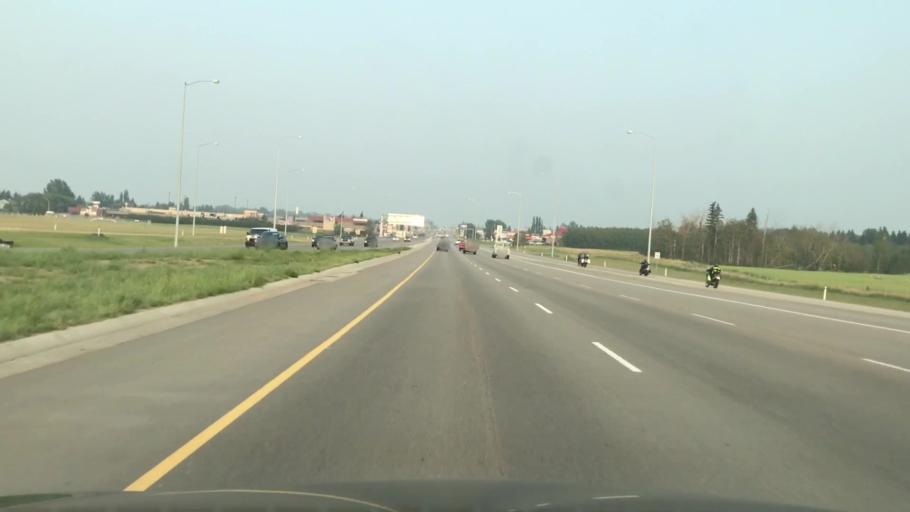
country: CA
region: Alberta
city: Sherwood Park
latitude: 53.5120
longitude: -113.3385
